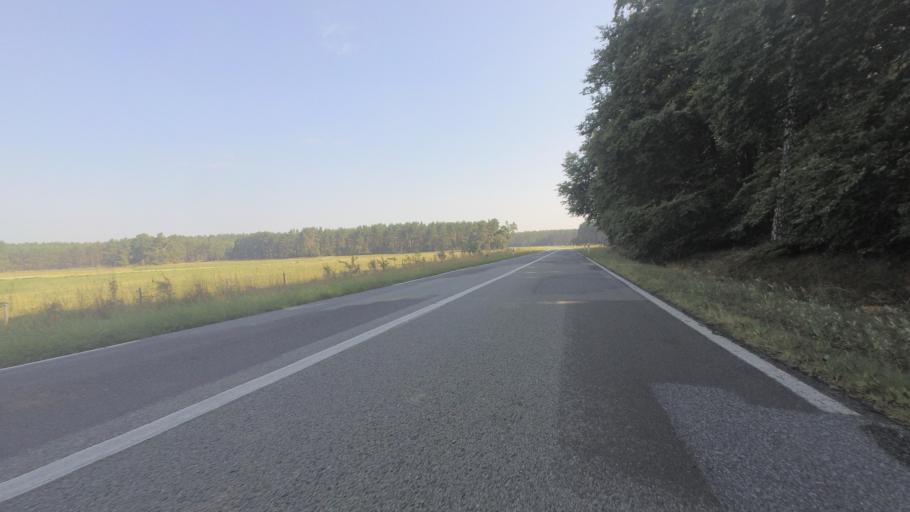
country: DE
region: Mecklenburg-Vorpommern
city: Malchow
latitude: 53.5390
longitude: 12.4296
